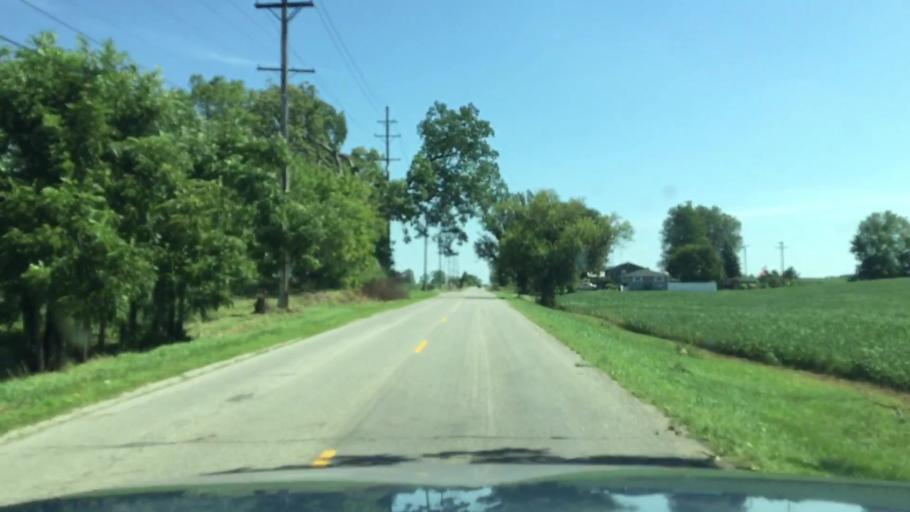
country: US
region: Michigan
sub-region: Lenawee County
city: Clinton
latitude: 42.0650
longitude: -83.9592
